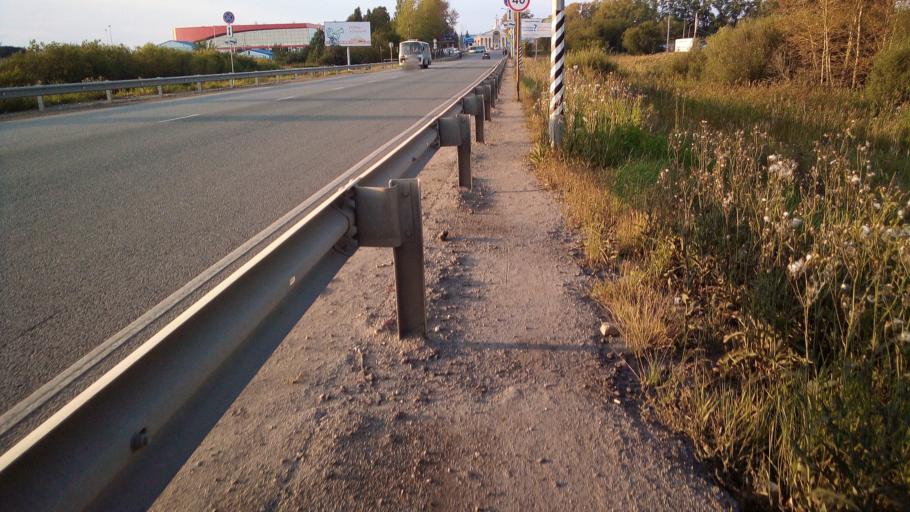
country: RU
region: Chelyabinsk
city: Potanino
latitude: 55.2927
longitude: 61.5114
